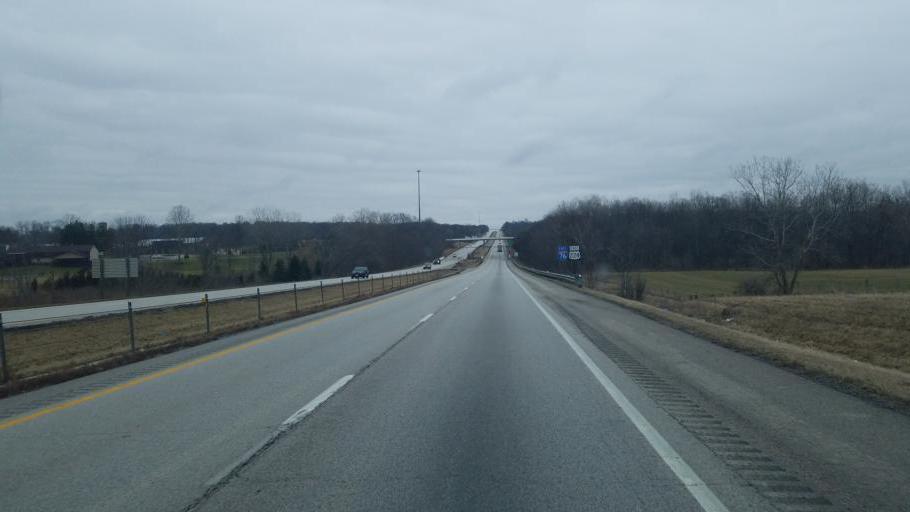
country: US
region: Ohio
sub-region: Medina County
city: Seville
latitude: 41.0327
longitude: -81.8555
